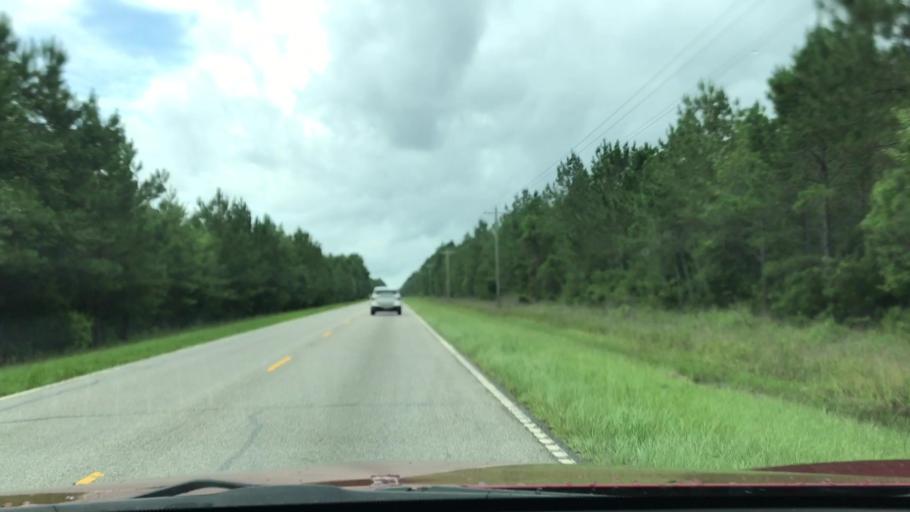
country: US
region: South Carolina
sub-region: Georgetown County
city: Murrells Inlet
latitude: 33.5940
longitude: -79.2029
